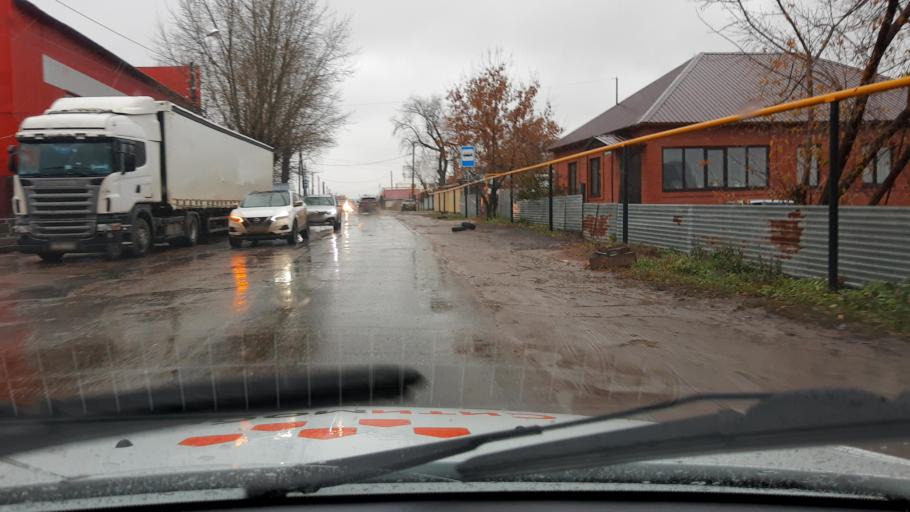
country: RU
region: Bashkortostan
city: Mikhaylovka
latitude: 54.6964
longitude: 55.8493
